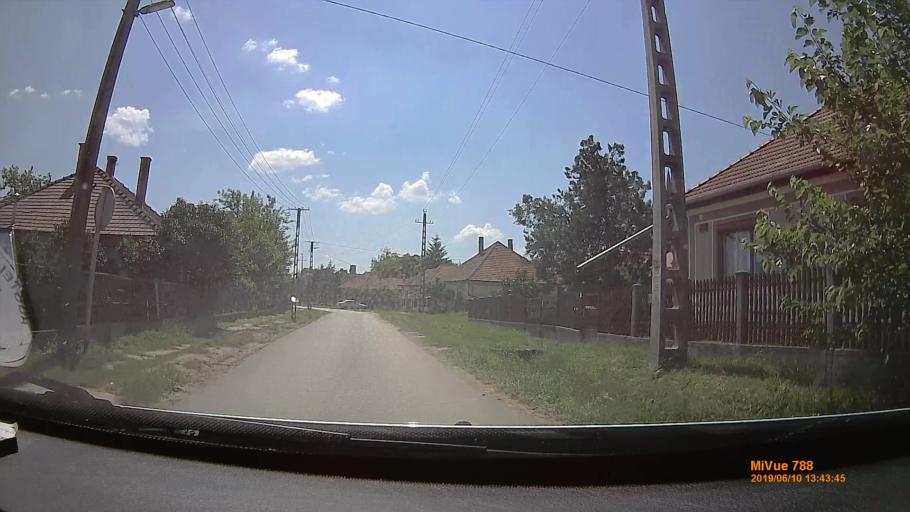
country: HU
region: Szabolcs-Szatmar-Bereg
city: Tiszadob
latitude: 48.0144
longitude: 21.1692
